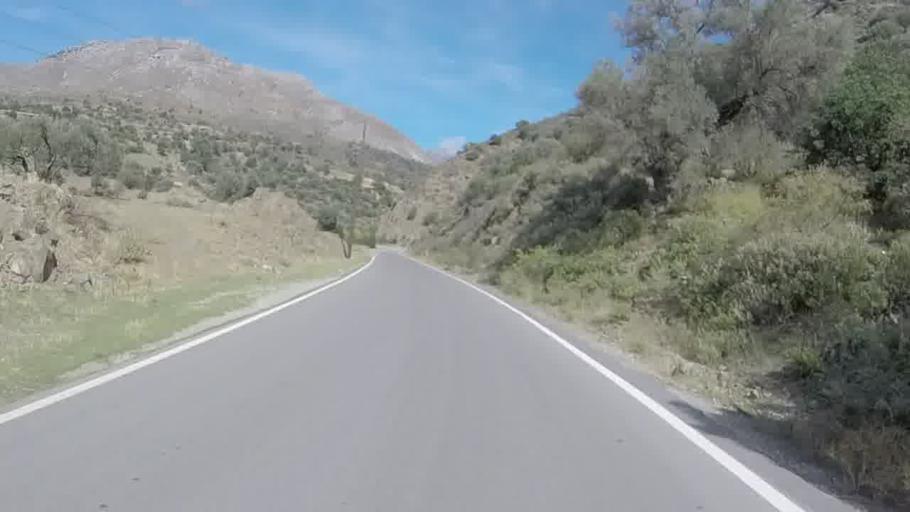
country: GR
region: Crete
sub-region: Nomos Rethymnis
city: Agia Galini
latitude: 35.1439
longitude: 24.7367
